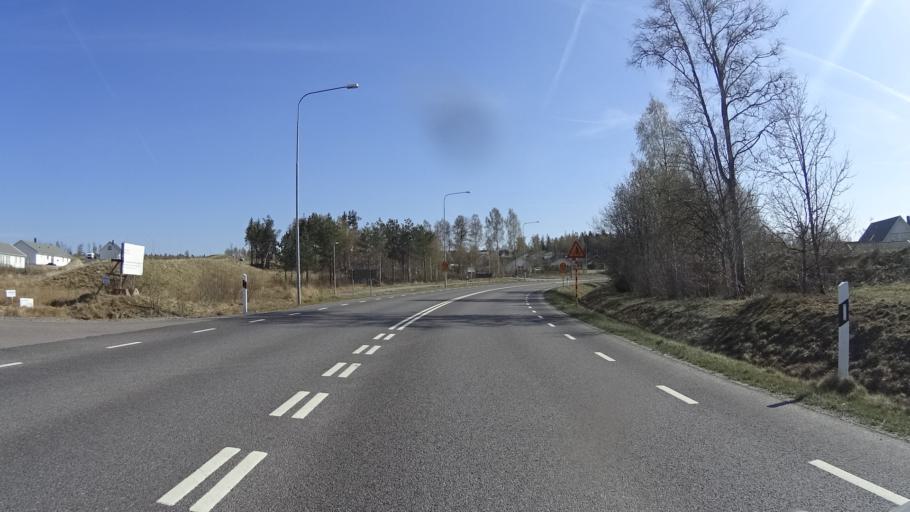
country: SE
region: Kronoberg
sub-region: Ljungby Kommun
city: Ljungby
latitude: 56.8412
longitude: 13.9743
